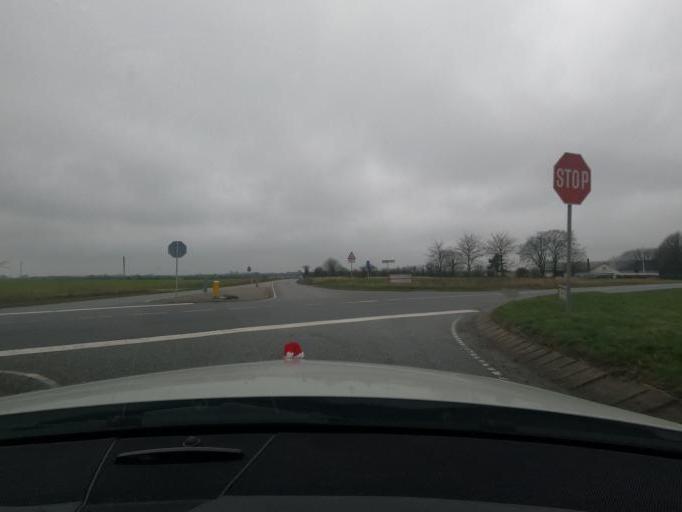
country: DK
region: South Denmark
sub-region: Haderslev Kommune
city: Starup
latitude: 55.2007
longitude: 9.5400
